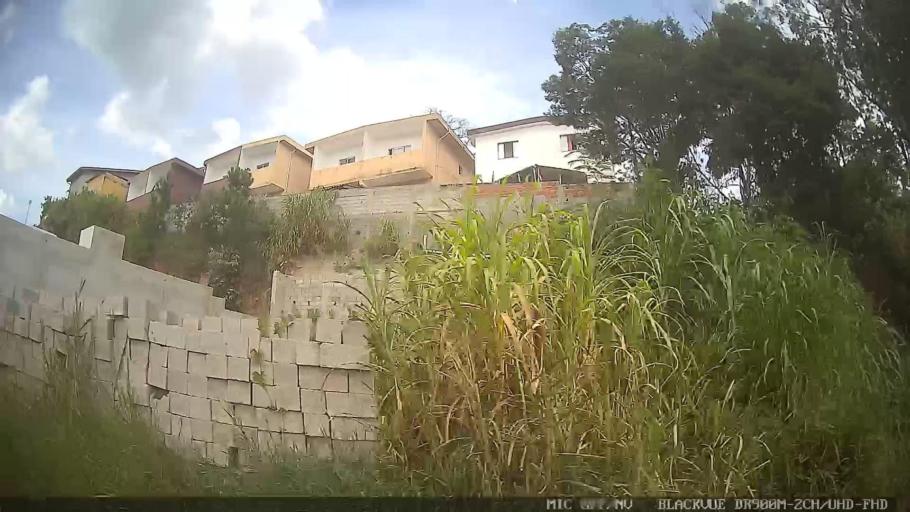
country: BR
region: Sao Paulo
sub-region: Atibaia
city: Atibaia
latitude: -23.0831
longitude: -46.5630
